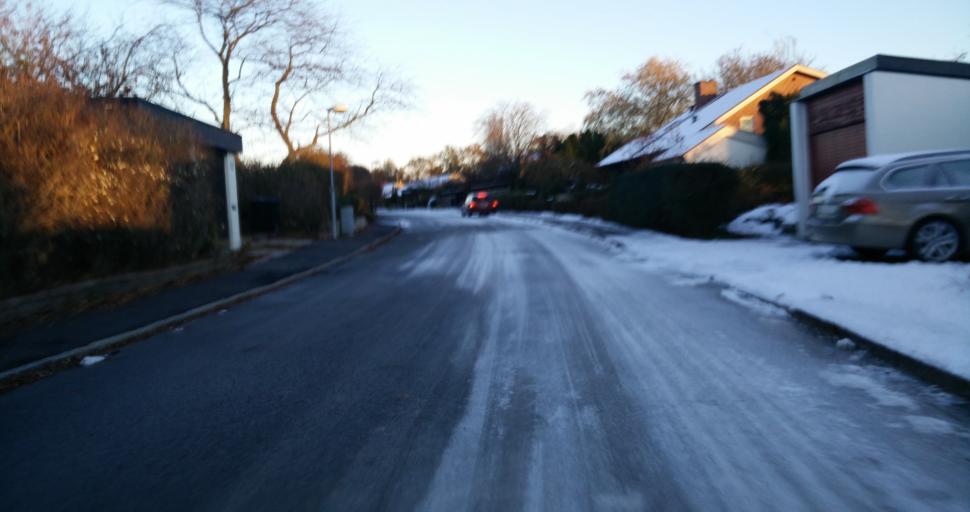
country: SE
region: Skane
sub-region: Lunds Kommun
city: Lund
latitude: 55.7035
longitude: 13.2146
